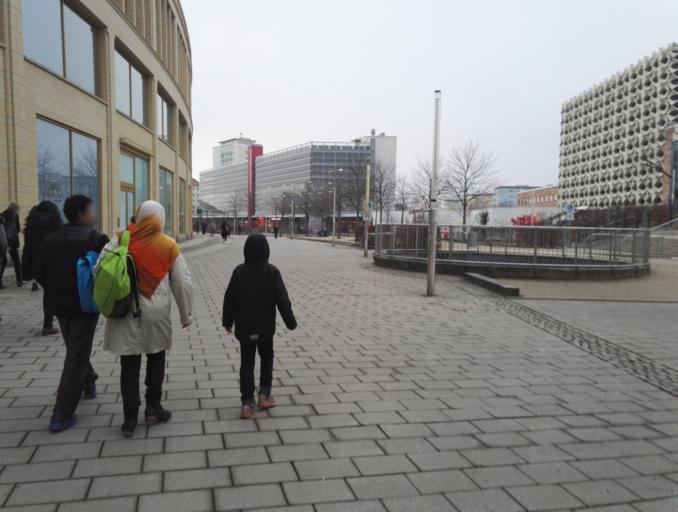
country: DE
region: Saxony
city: Chemnitz
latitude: 50.8343
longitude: 12.9214
